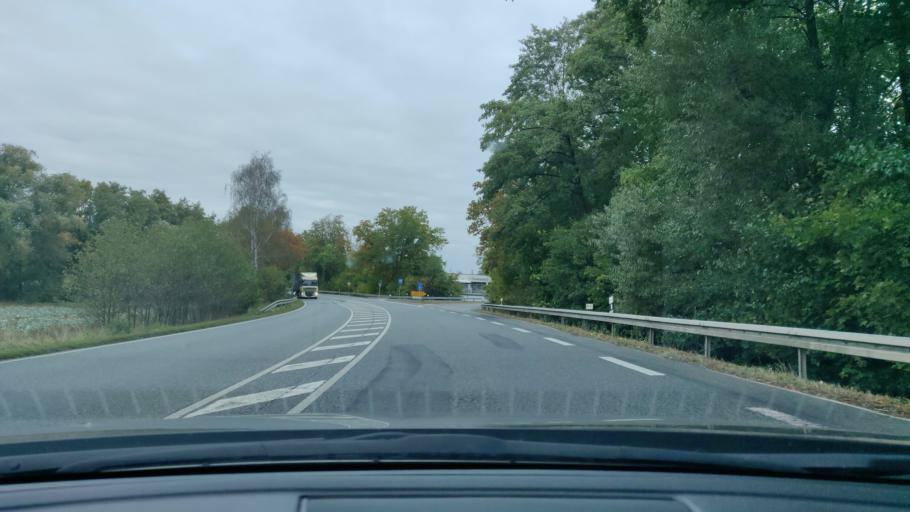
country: DE
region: Hesse
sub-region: Regierungsbezirk Kassel
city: Frielendorf
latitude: 50.9726
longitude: 9.3150
